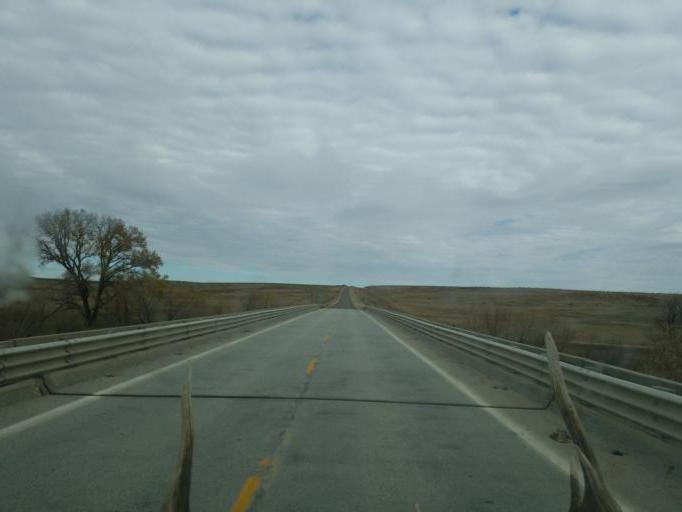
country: US
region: Kansas
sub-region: Wallace County
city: Sharon Springs
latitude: 39.0176
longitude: -101.3484
